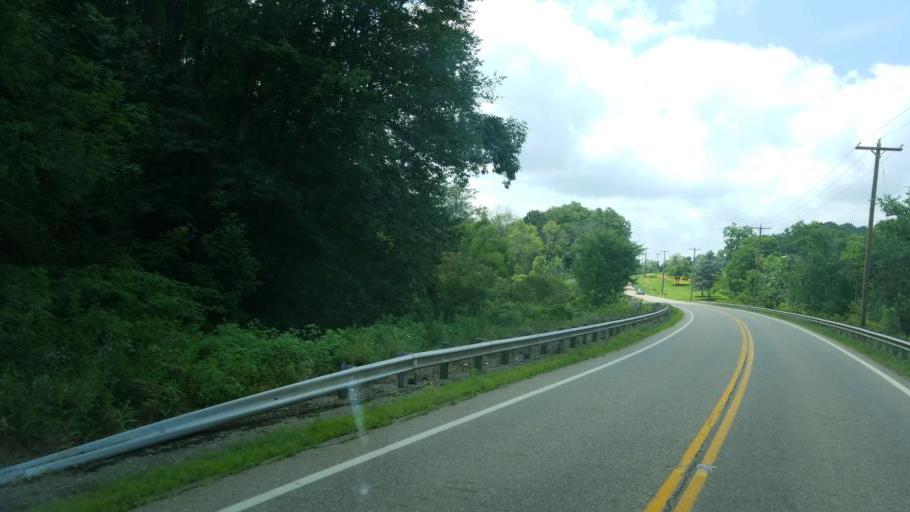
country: US
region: Ohio
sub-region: Columbiana County
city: Salem
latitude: 40.7956
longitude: -80.9094
